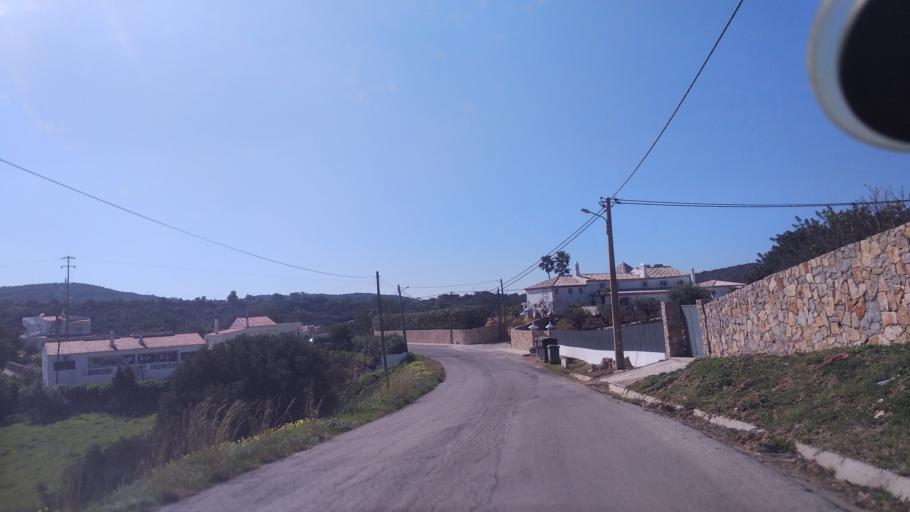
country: PT
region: Faro
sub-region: Faro
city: Santa Barbara de Nexe
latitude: 37.1123
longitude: -7.9331
